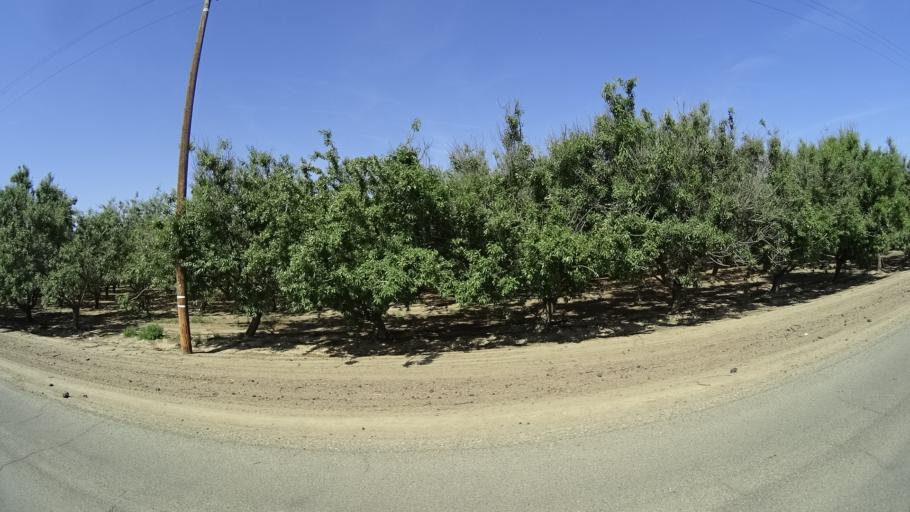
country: US
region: California
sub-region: Kings County
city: Kettleman City
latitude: 36.0679
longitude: -120.0037
